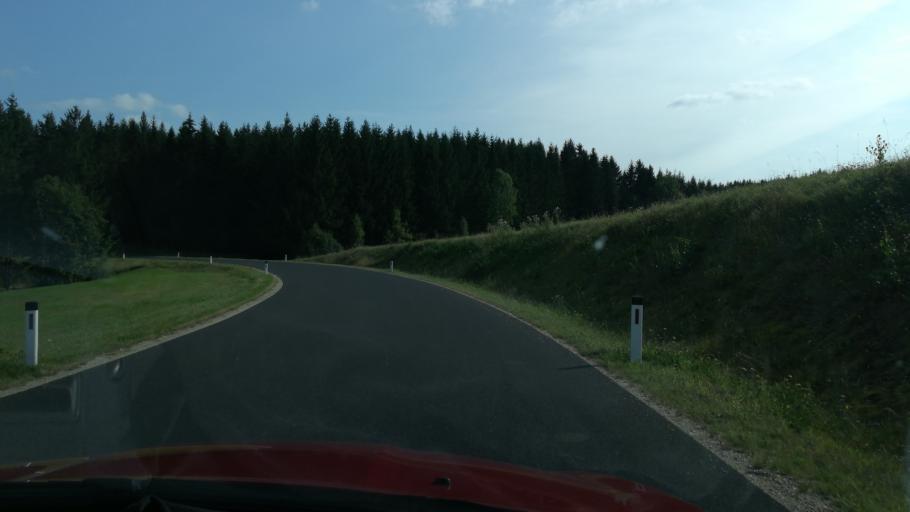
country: AT
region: Lower Austria
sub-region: Politischer Bezirk Zwettl
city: Langschlag
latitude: 48.5071
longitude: 14.8426
